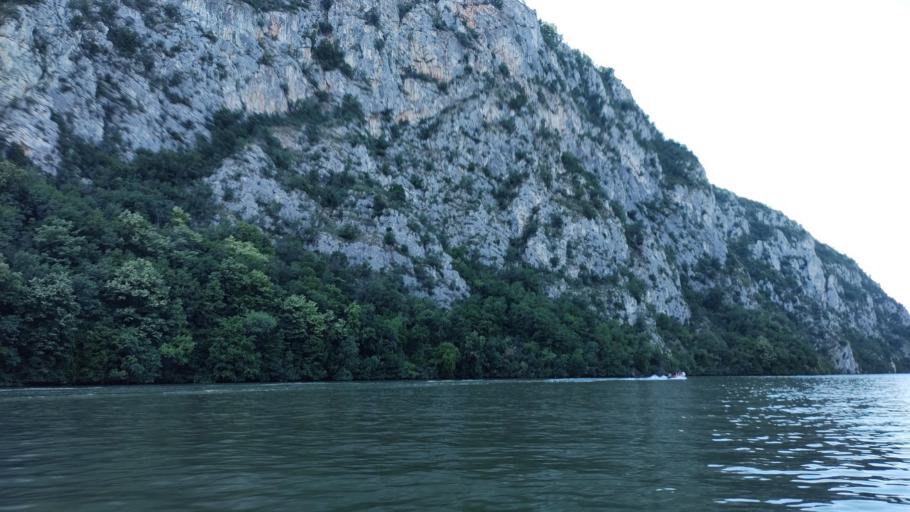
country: RO
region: Mehedinti
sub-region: Comuna Dubova
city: Dubova
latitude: 44.6060
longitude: 22.2684
